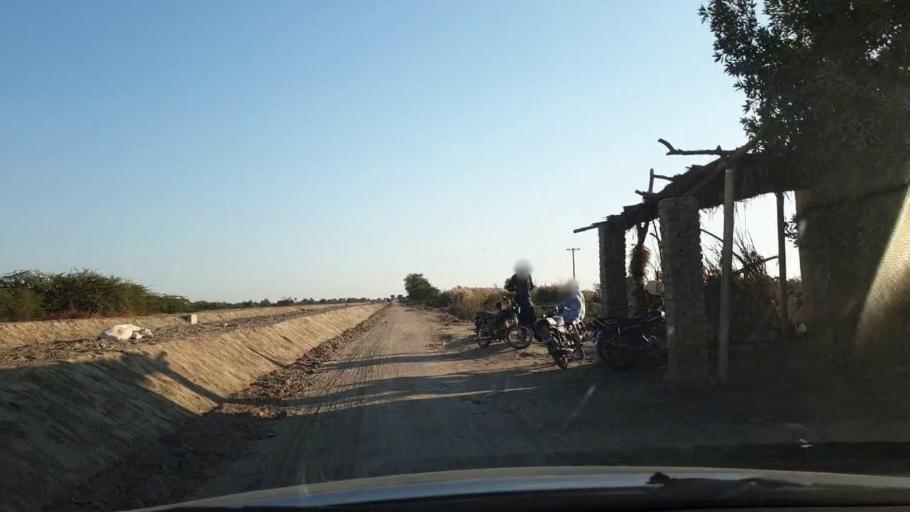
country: PK
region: Sindh
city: Tando Mittha Khan
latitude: 25.8396
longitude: 69.1730
